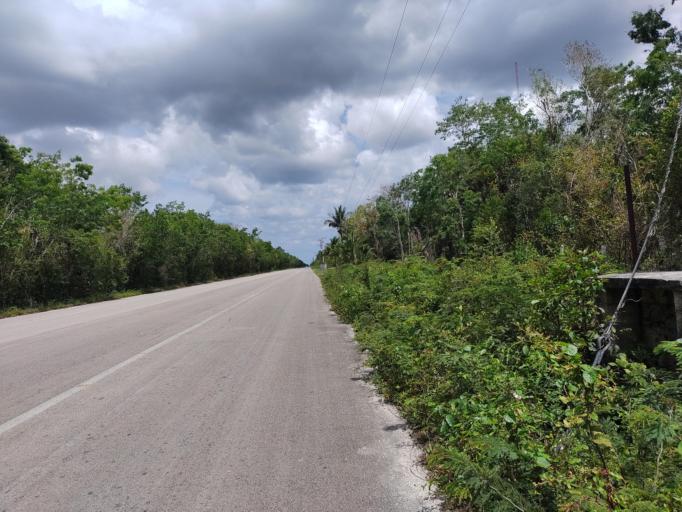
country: MX
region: Quintana Roo
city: San Miguel de Cozumel
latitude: 20.4713
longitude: -86.9010
